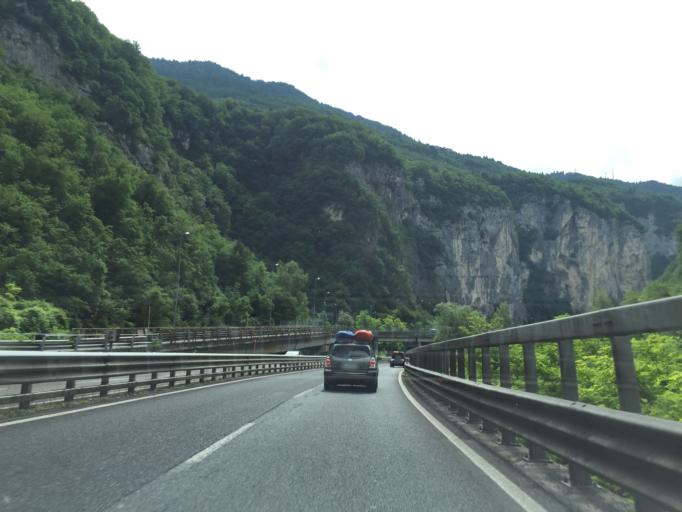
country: IT
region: Veneto
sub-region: Provincia di Vicenza
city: Enego
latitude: 45.9543
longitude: 11.7187
